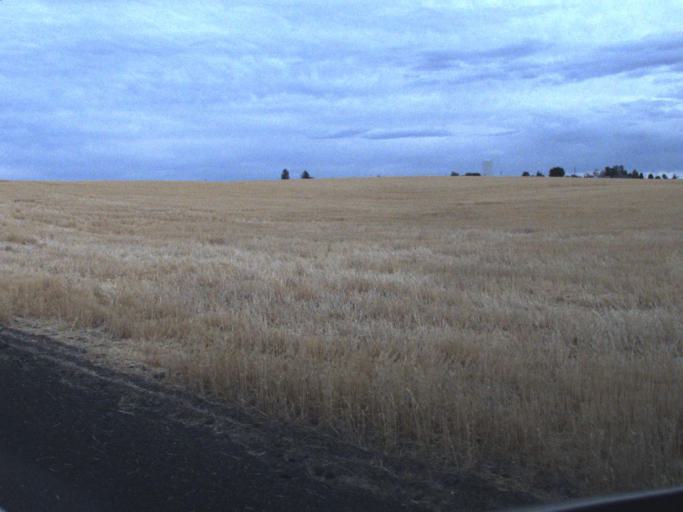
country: US
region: Washington
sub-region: Okanogan County
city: Coulee Dam
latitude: 47.7446
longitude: -118.7218
